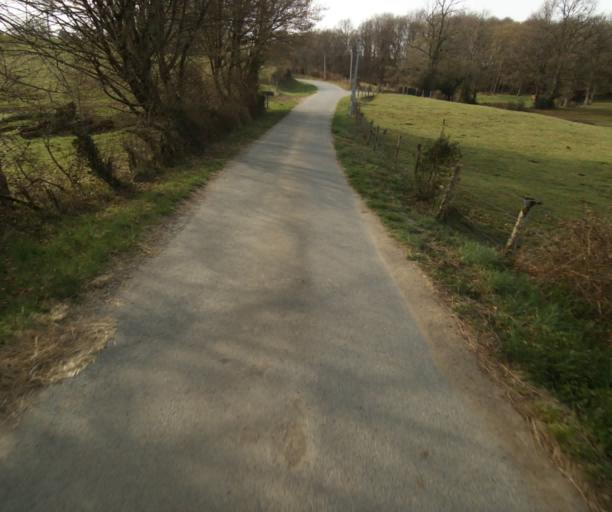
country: FR
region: Limousin
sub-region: Departement de la Correze
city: Chamboulive
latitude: 45.4440
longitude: 1.7538
